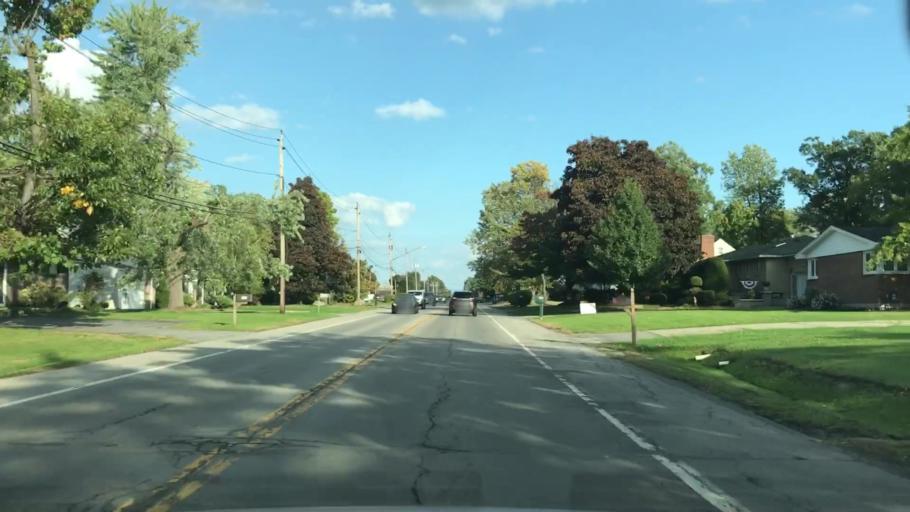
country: US
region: New York
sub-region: Erie County
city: Williamsville
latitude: 42.9496
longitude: -78.7509
